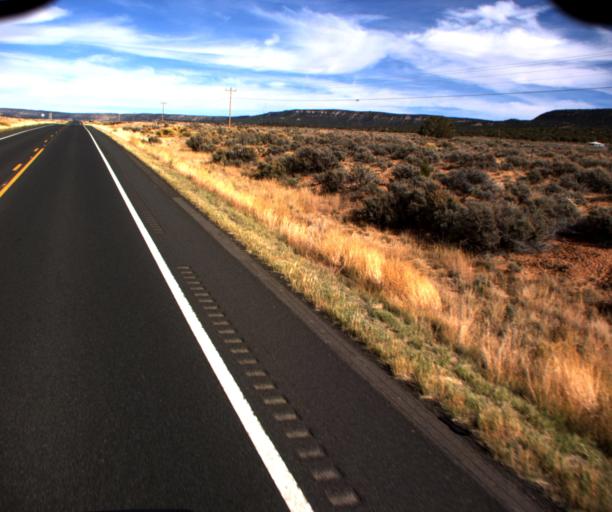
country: US
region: Arizona
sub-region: Navajo County
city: Kayenta
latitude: 36.5241
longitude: -110.5802
